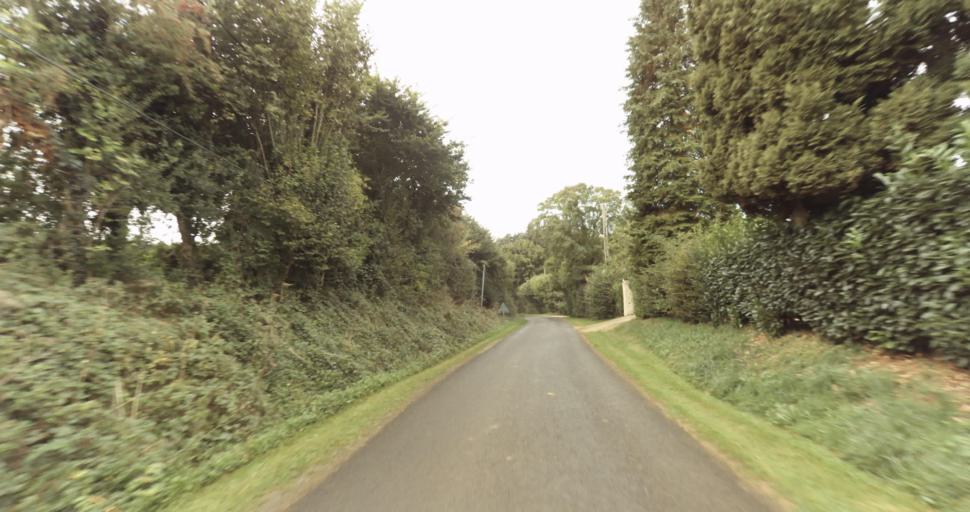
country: FR
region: Lower Normandy
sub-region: Departement de l'Orne
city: Sainte-Gauburge-Sainte-Colombe
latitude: 48.7315
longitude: 0.3785
